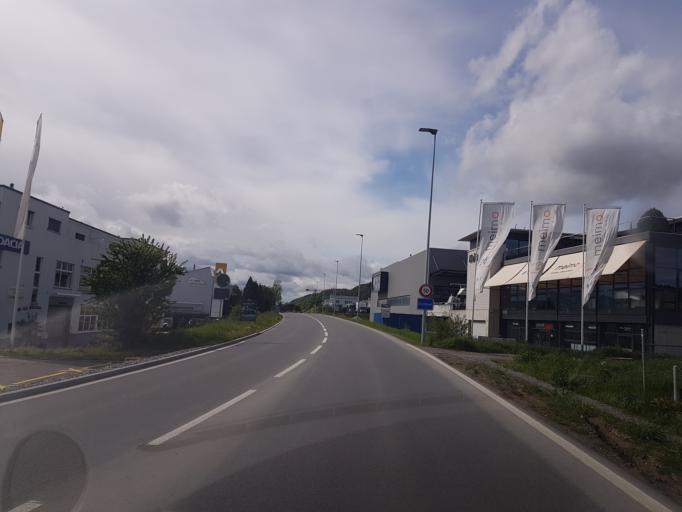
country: CH
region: Zurich
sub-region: Bezirk Dietikon
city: Geroldswil
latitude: 47.4179
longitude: 8.4181
